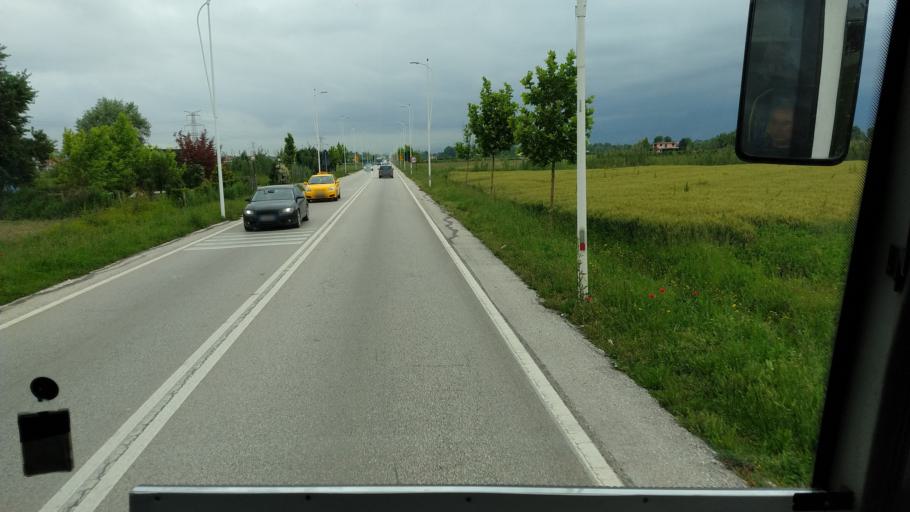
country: AL
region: Tirane
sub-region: Rrethi i Tiranes
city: Berxull
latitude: 41.3797
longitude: 19.7037
